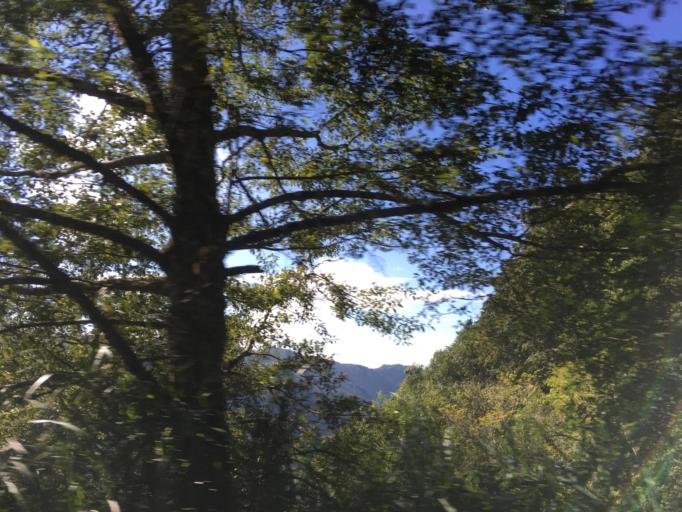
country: TW
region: Taiwan
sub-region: Yilan
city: Yilan
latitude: 24.5091
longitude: 121.5695
